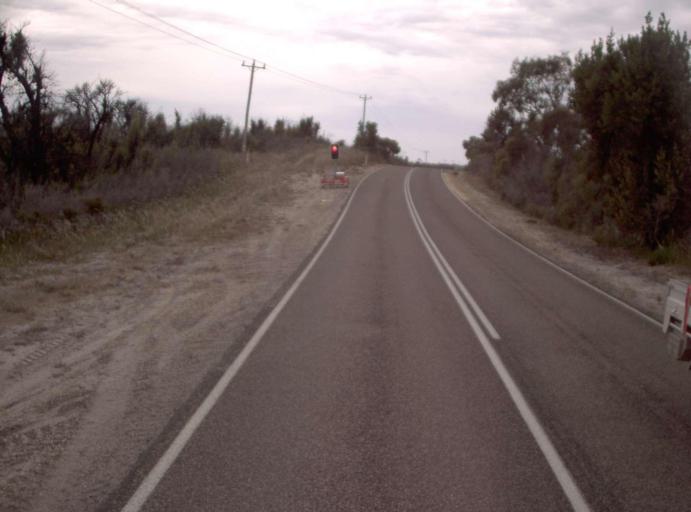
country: AU
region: Victoria
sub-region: East Gippsland
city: Bairnsdale
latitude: -38.1038
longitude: 147.4899
